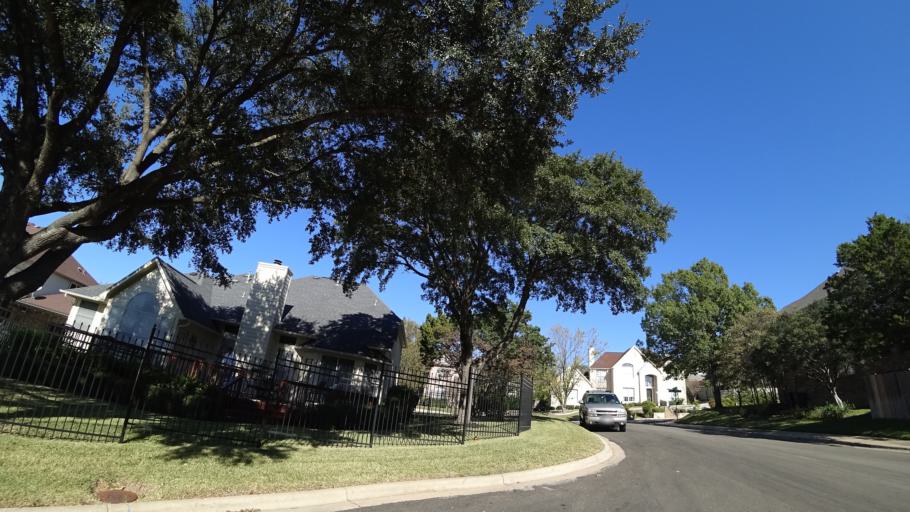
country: US
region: Texas
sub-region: Williamson County
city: Jollyville
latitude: 30.4117
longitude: -97.7706
